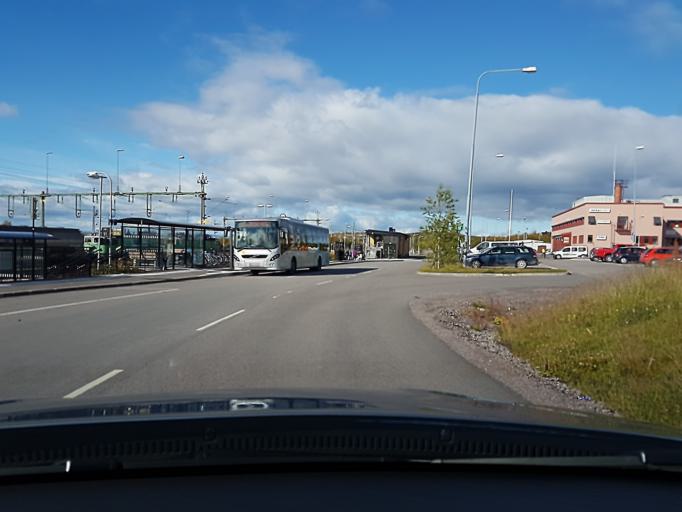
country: SE
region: Norrbotten
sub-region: Kiruna Kommun
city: Kiruna
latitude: 67.8675
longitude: 20.2008
